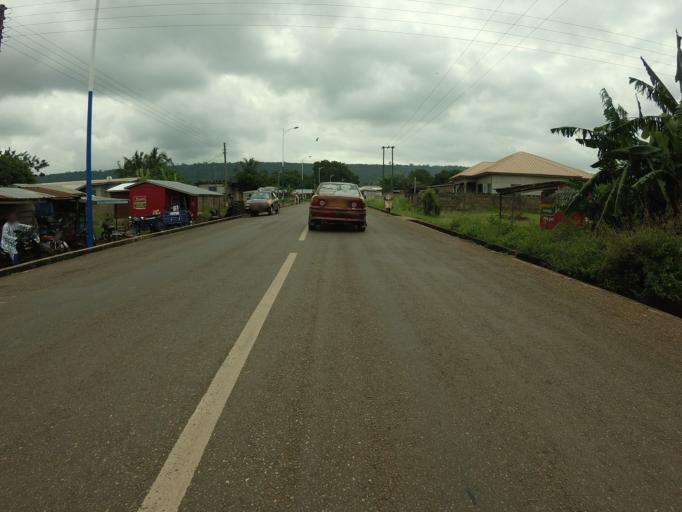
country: GH
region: Volta
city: Ho
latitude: 6.6296
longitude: 0.4879
